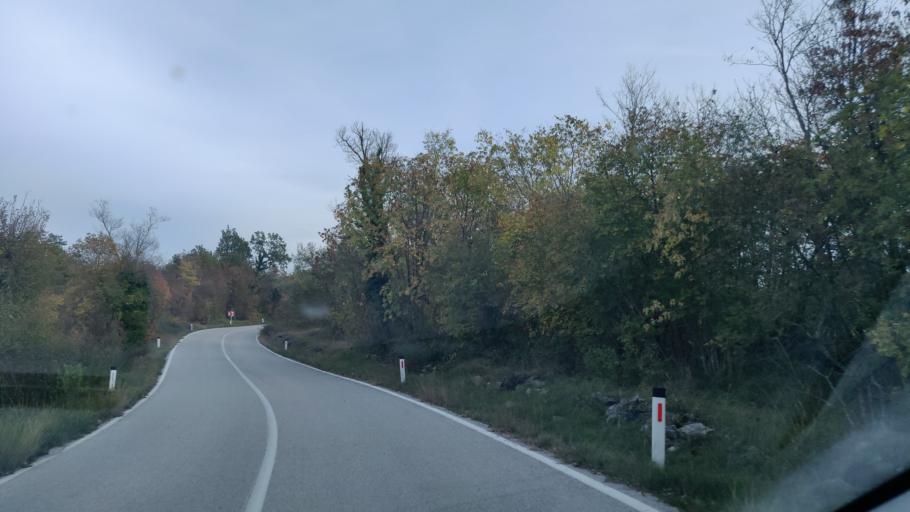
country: SI
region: Rence-Vogrsko
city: Rence
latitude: 45.8388
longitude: 13.6479
